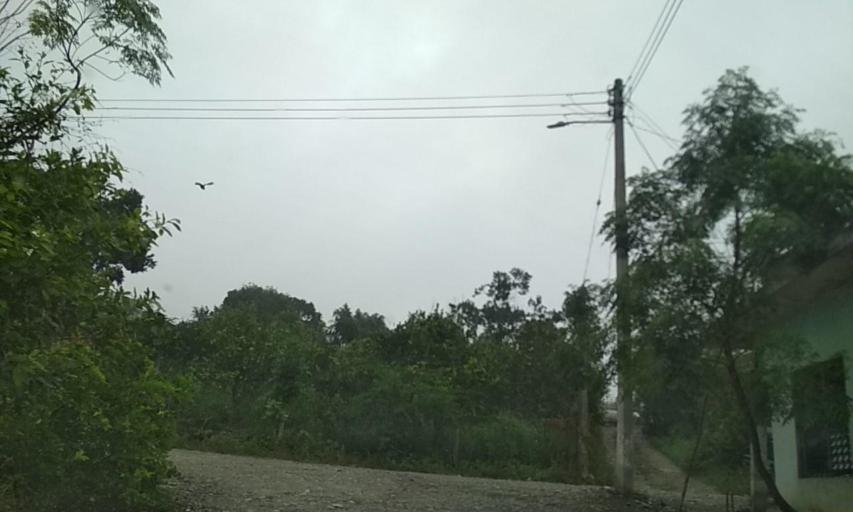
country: MX
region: Puebla
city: Espinal
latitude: 20.3289
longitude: -97.3926
